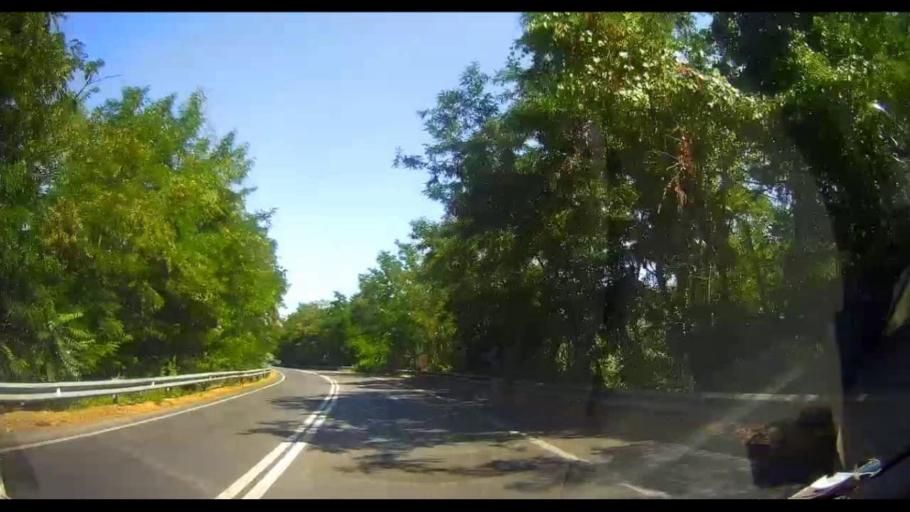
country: IT
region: Calabria
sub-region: Provincia di Cosenza
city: Cosenza
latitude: 39.2986
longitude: 16.2649
